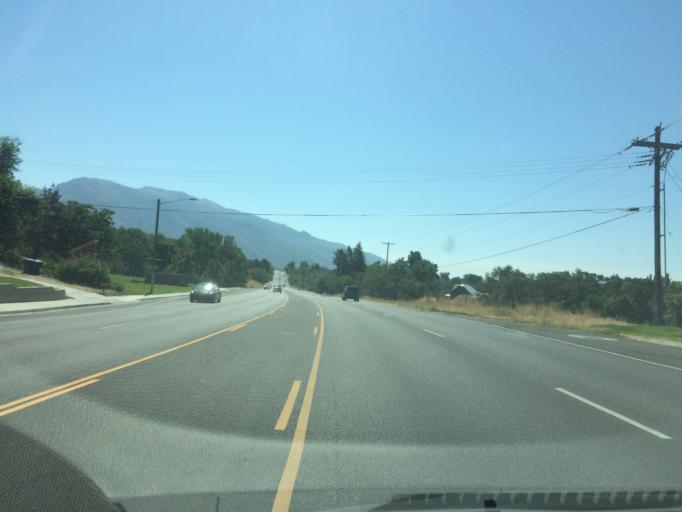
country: US
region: Utah
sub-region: Weber County
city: Washington Terrace
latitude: 41.1729
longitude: -111.9488
